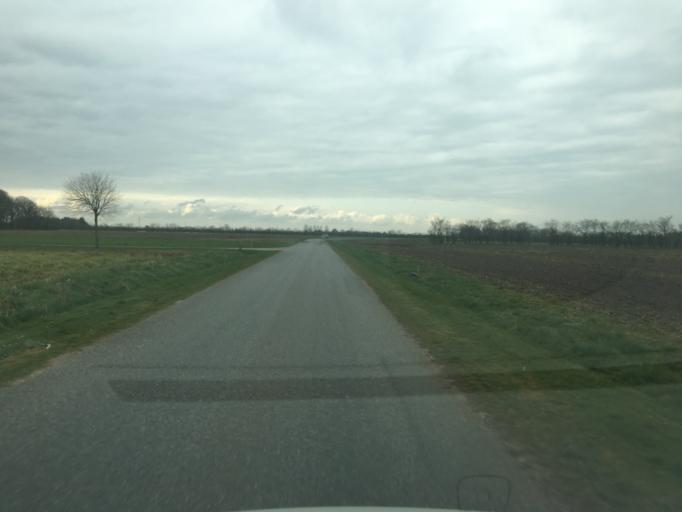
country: DK
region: South Denmark
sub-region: Aabenraa Kommune
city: Tinglev
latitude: 55.0450
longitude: 9.1417
